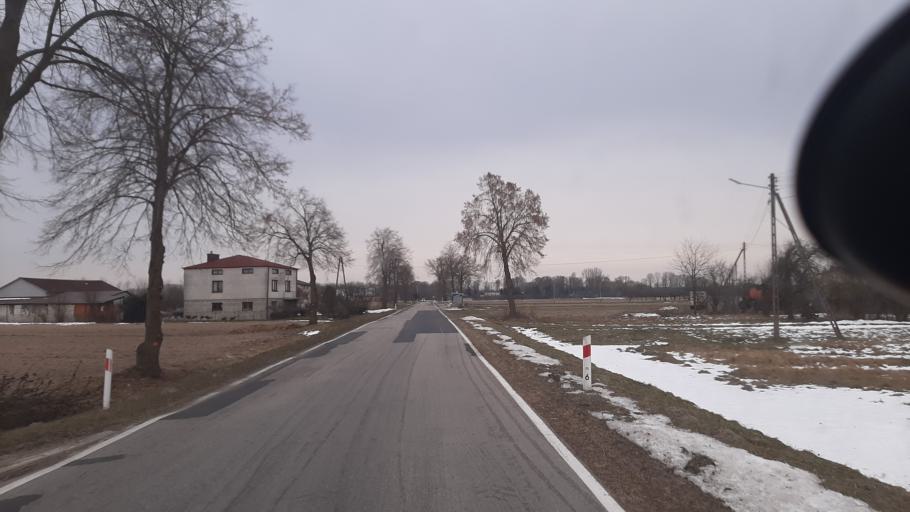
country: PL
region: Lublin Voivodeship
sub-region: Powiat lubartowski
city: Kamionka
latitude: 51.4543
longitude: 22.4211
